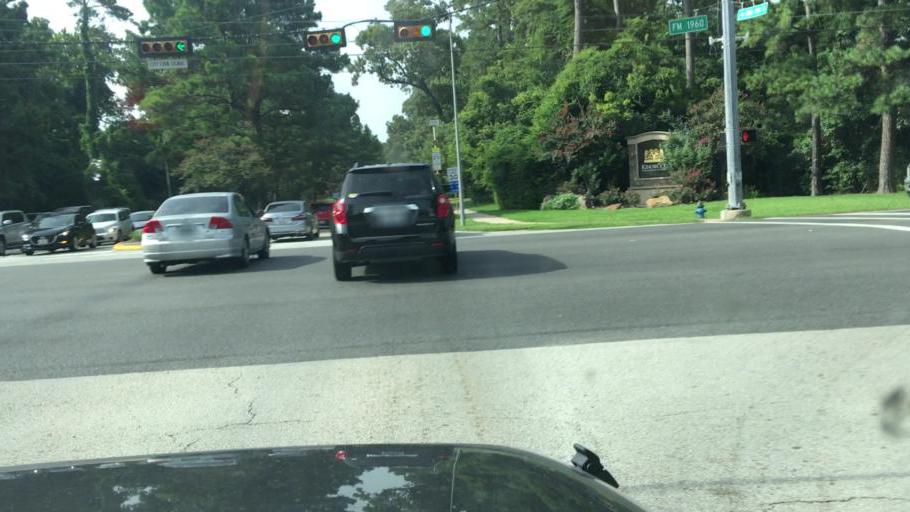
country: US
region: Texas
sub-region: Harris County
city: Atascocita
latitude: 29.9984
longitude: -95.1781
